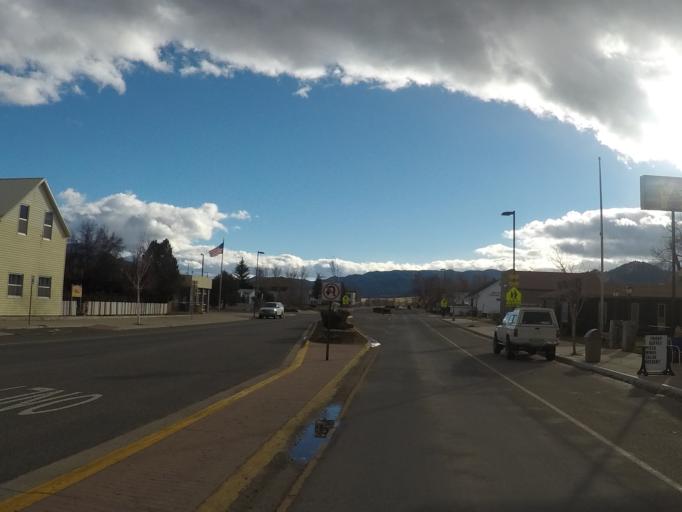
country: US
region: Montana
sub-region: Jefferson County
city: Boulder
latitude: 46.2363
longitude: -112.1194
